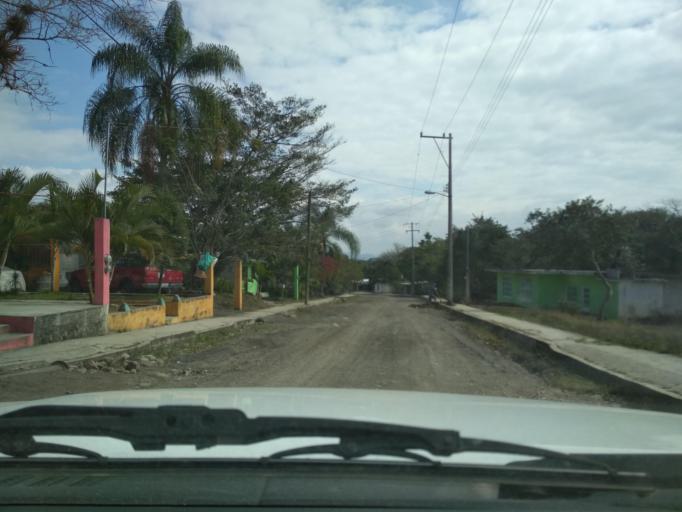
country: MX
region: Veracruz
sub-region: Coatepec
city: Tuzamapan
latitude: 19.3709
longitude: -96.8788
